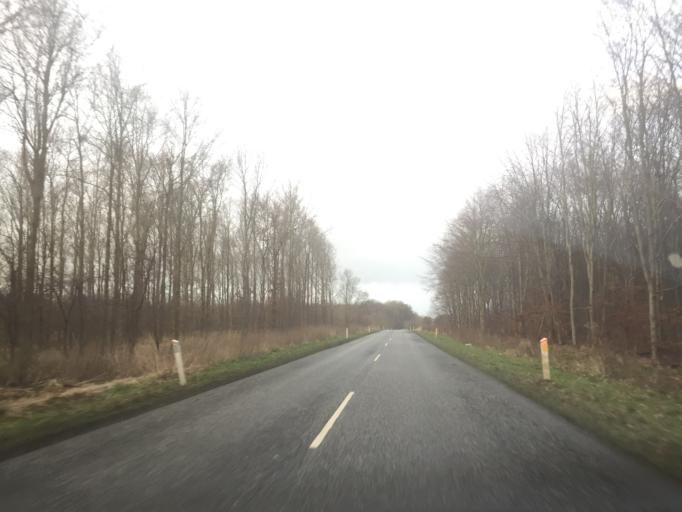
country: DK
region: Capital Region
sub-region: Egedal Kommune
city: Smorumnedre
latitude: 55.6944
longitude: 12.3229
